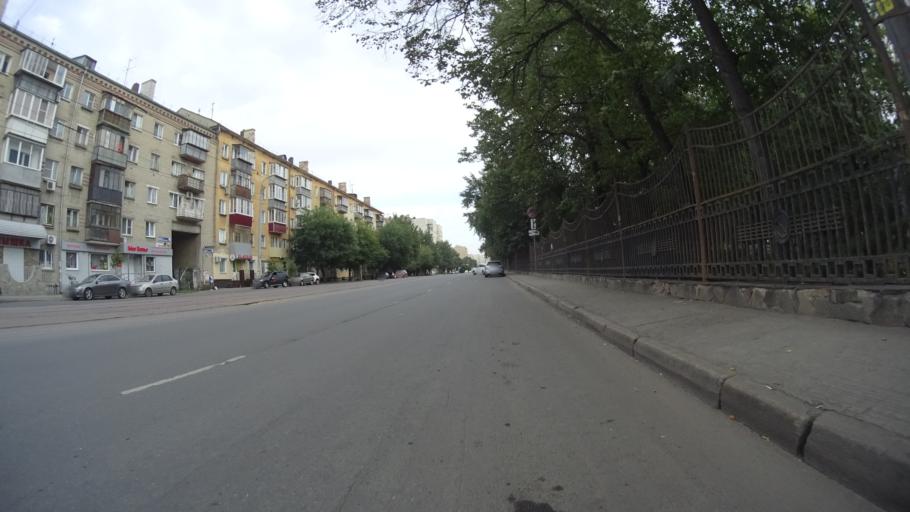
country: RU
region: Chelyabinsk
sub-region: Gorod Chelyabinsk
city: Chelyabinsk
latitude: 55.1546
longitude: 61.4072
